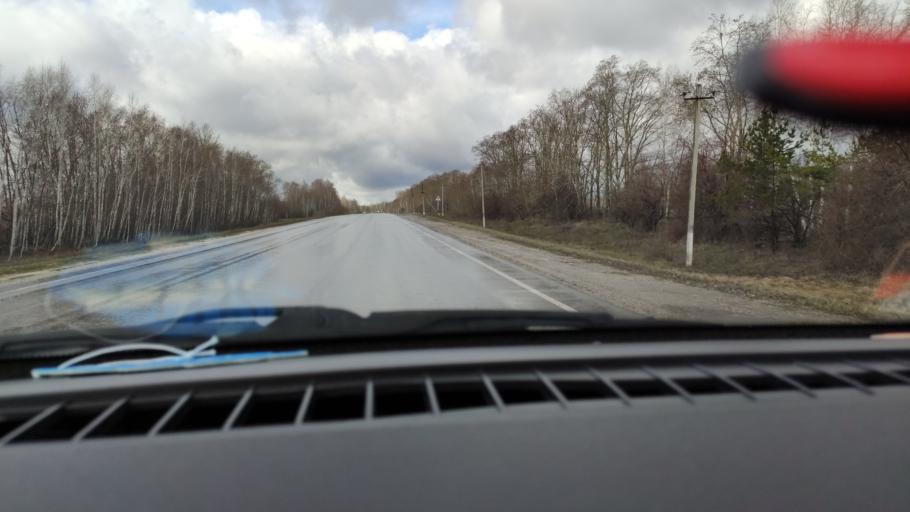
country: RU
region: Samara
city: Yelkhovka
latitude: 54.0582
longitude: 50.3003
